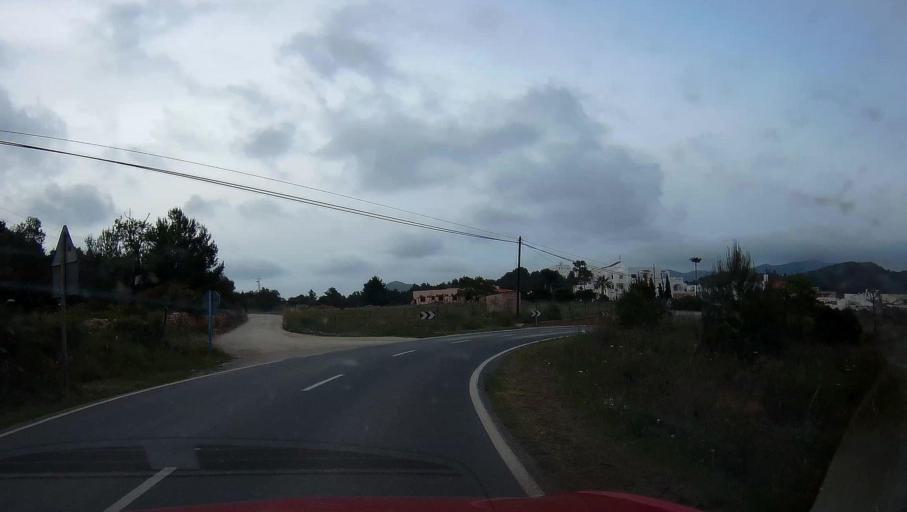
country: ES
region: Balearic Islands
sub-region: Illes Balears
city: Sant Joan de Labritja
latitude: 39.0524
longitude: 1.4342
